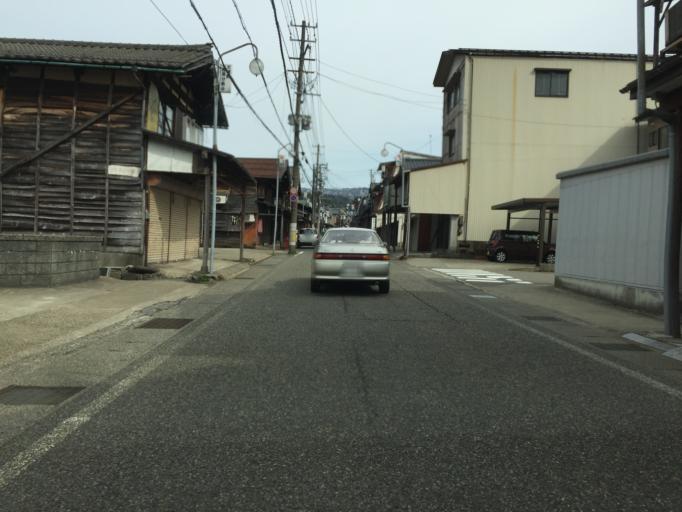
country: JP
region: Niigata
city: Tochio-honcho
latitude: 37.4727
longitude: 138.9983
